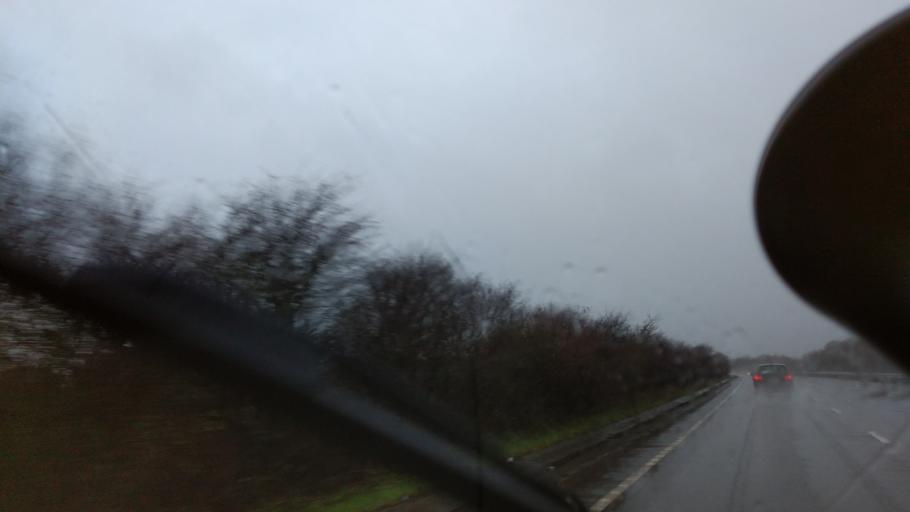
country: GB
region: England
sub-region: West Sussex
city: Rustington
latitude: 50.8400
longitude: -0.4703
